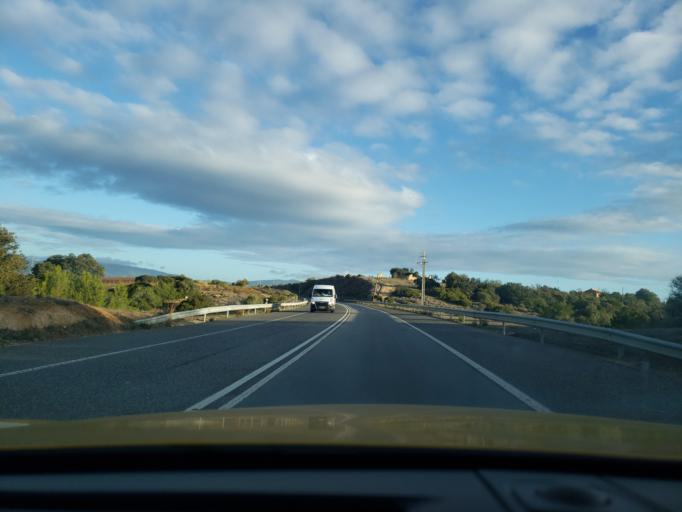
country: PT
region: Faro
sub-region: Portimao
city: Portimao
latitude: 37.1700
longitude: -8.5678
